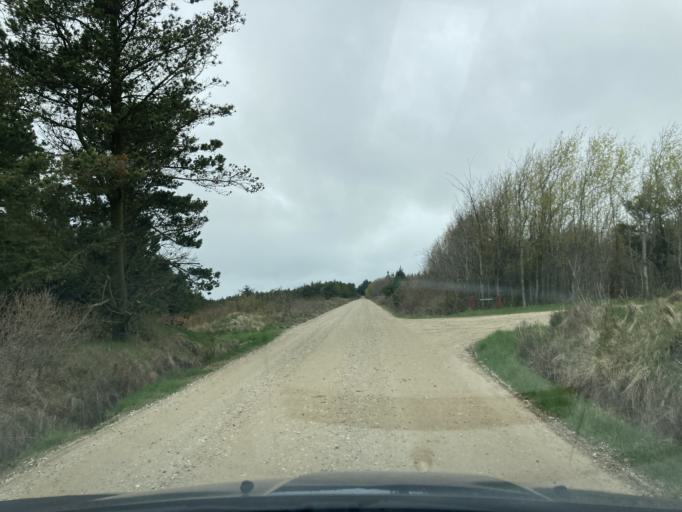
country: DK
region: Central Jutland
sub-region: Lemvig Kommune
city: Thyboron
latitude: 56.8177
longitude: 8.2742
